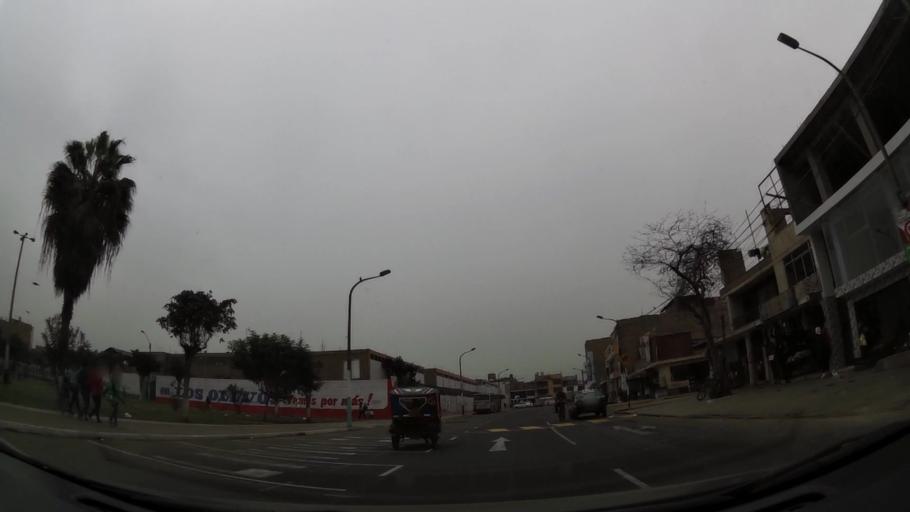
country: PE
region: Lima
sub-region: Lima
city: Independencia
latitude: -11.9358
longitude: -77.0757
